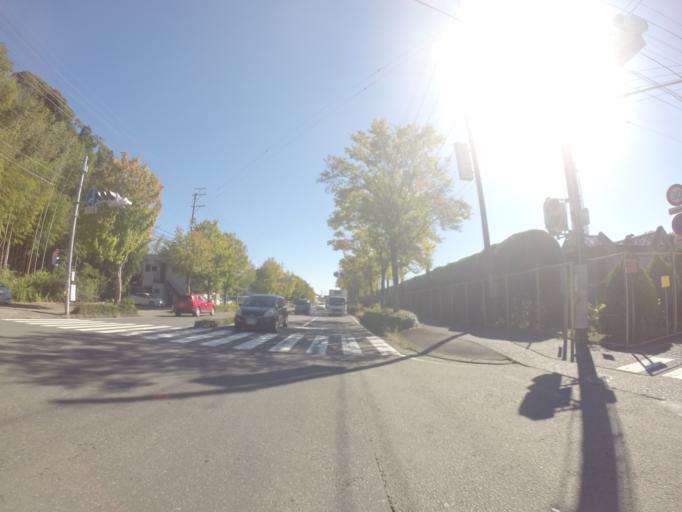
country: JP
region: Shizuoka
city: Fujieda
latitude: 34.8669
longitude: 138.2337
